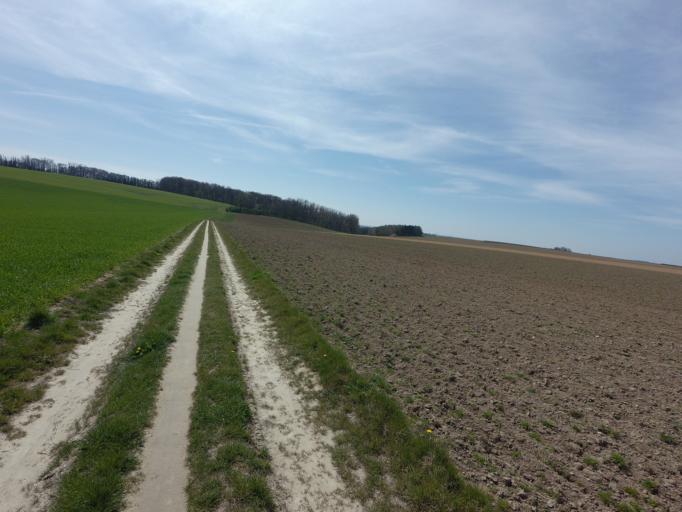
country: NL
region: Limburg
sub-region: Eijsden-Margraten
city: Eijsden
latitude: 50.7823
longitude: 5.7693
